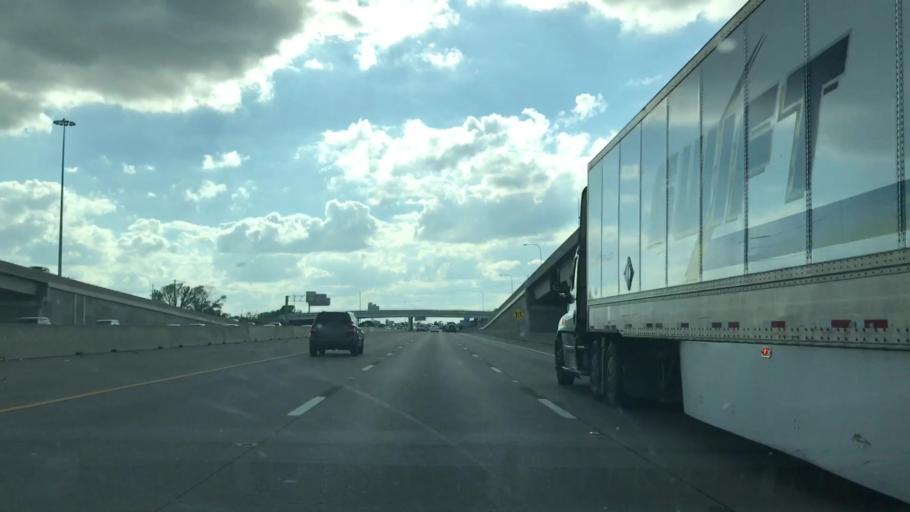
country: US
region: Texas
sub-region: Dallas County
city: Rowlett
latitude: 32.8549
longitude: -96.5589
